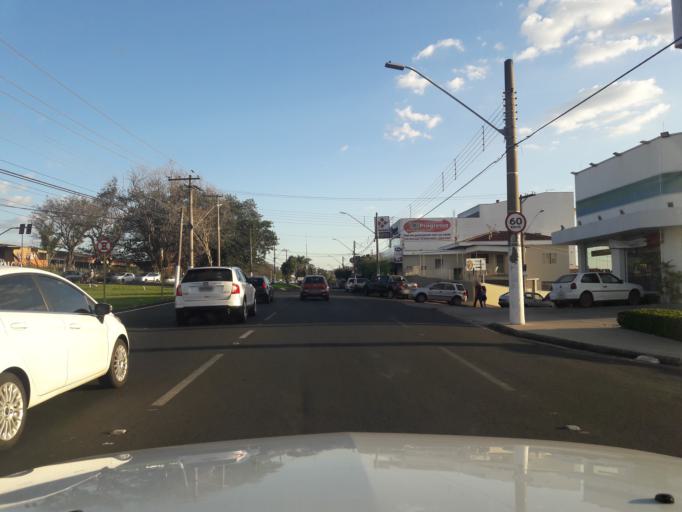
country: BR
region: Sao Paulo
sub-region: Moji-Guacu
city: Mogi-Gaucu
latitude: -22.3910
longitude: -46.9453
